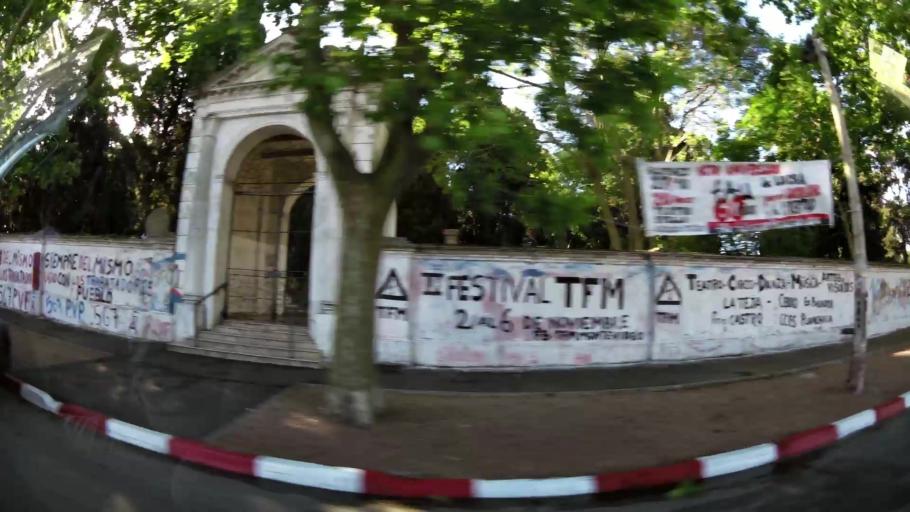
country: UY
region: Montevideo
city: Montevideo
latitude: -34.8592
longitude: -56.2277
